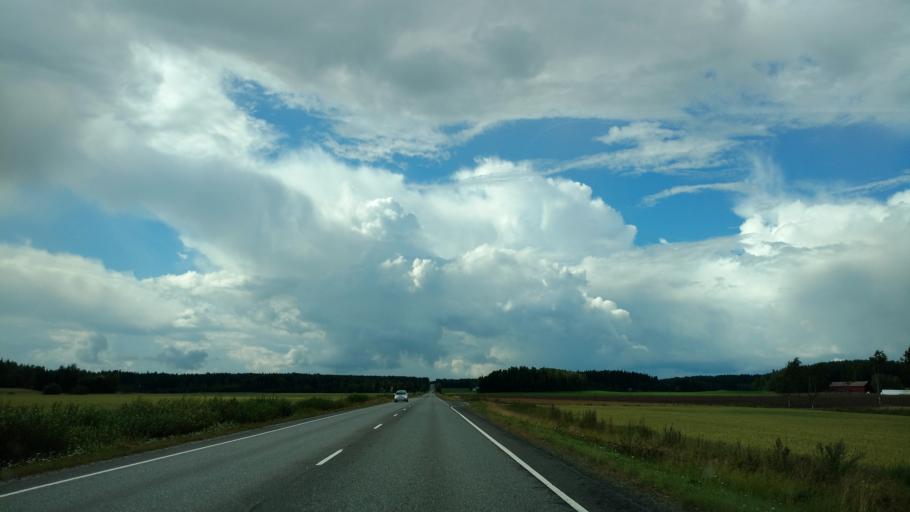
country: FI
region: Varsinais-Suomi
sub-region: Turku
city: Sauvo
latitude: 60.3918
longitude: 22.8660
